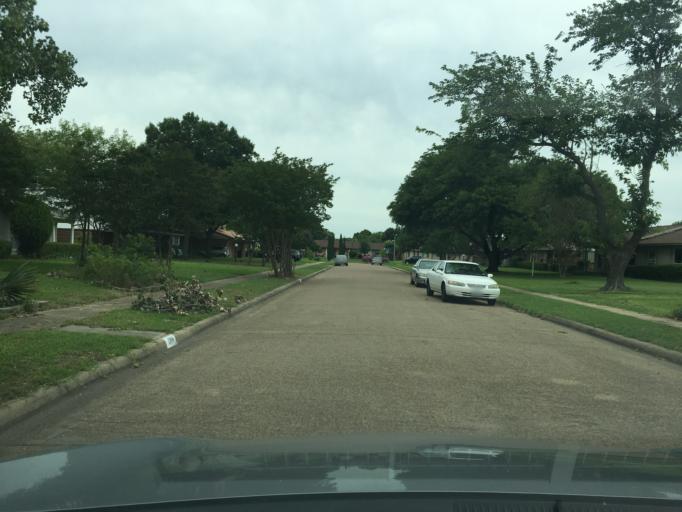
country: US
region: Texas
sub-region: Dallas County
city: Richardson
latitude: 32.9331
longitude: -96.7033
